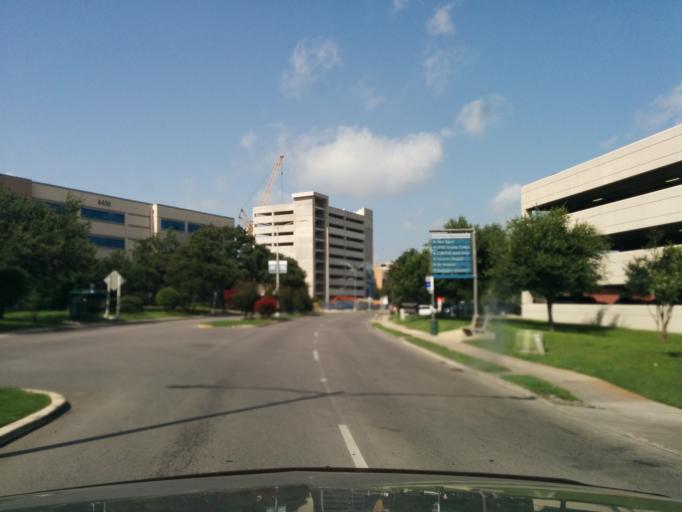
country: US
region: Texas
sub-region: Bexar County
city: Balcones Heights
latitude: 29.5100
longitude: -98.5720
